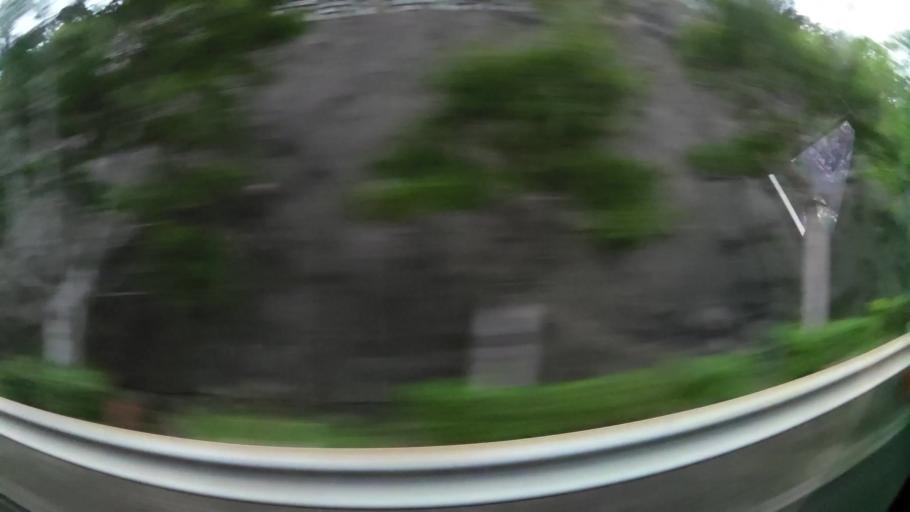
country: HK
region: Tsuen Wan
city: Tsuen Wan
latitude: 22.3570
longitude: 114.0839
